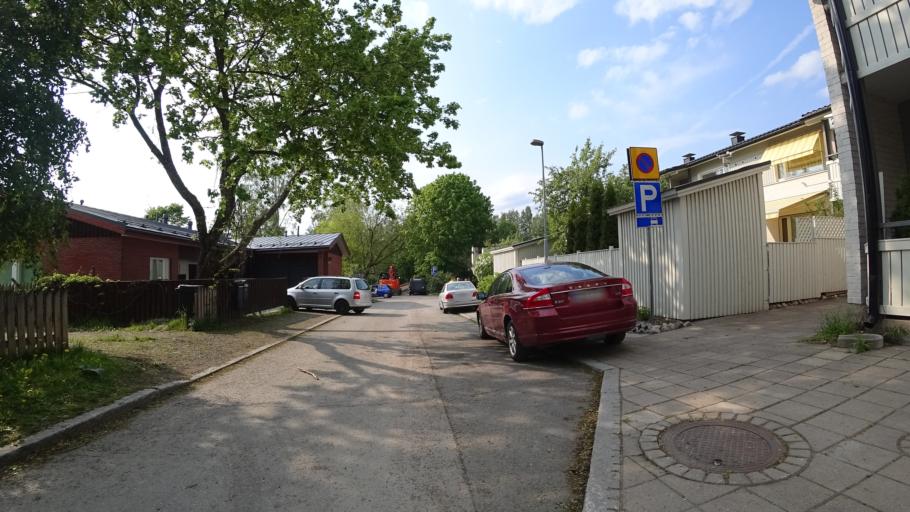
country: FI
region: Pirkanmaa
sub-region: Tampere
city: Tampere
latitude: 61.5004
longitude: 23.7116
